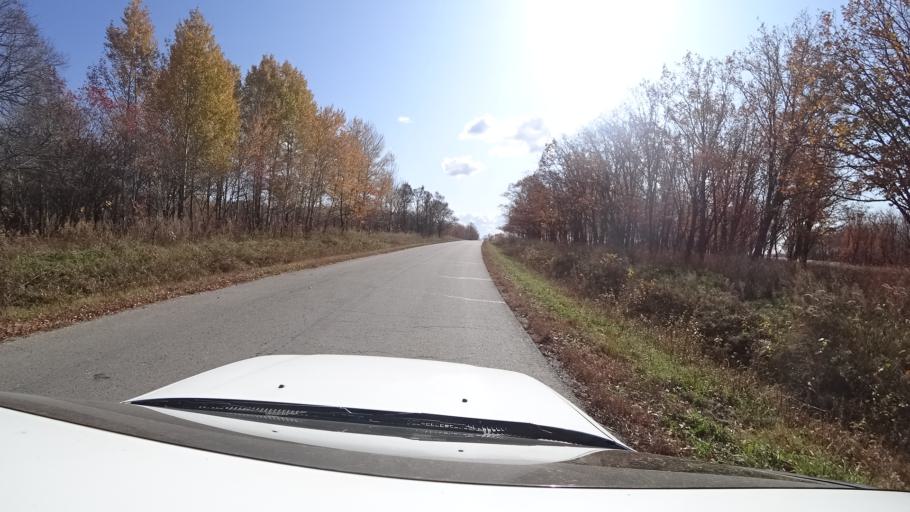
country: RU
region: Primorskiy
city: Lazo
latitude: 45.8699
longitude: 133.6606
